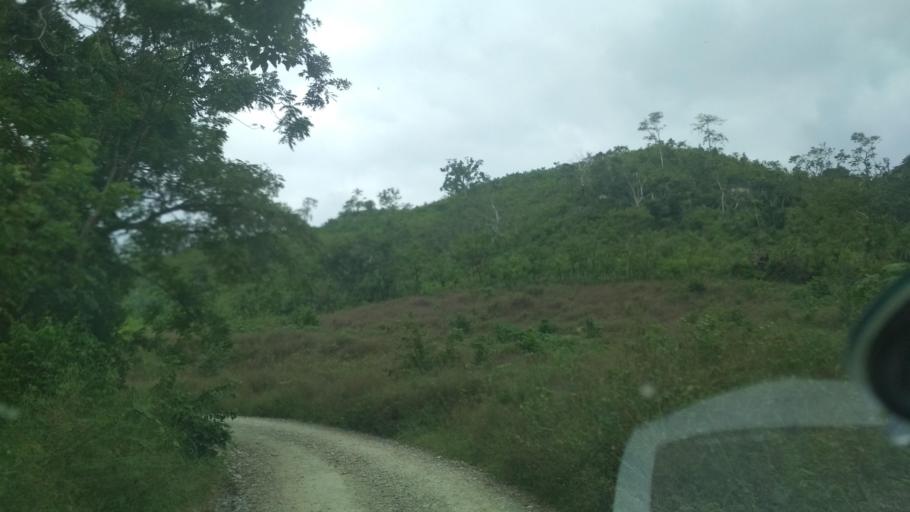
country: MX
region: Veracruz
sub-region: Poza Rica de Hidalgo
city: El Mollejon
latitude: 20.5260
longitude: -97.3886
